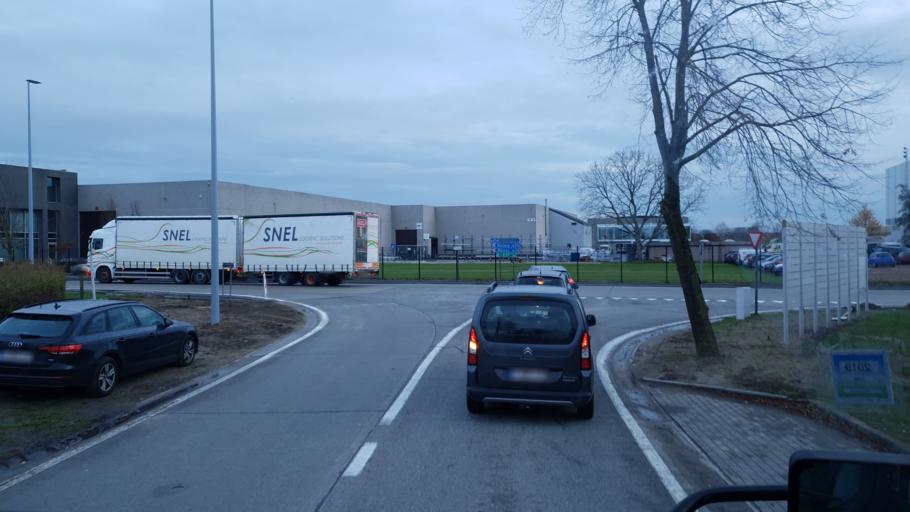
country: BE
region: Flanders
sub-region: Provincie Oost-Vlaanderen
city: Deinze
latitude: 50.9597
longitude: 3.5509
